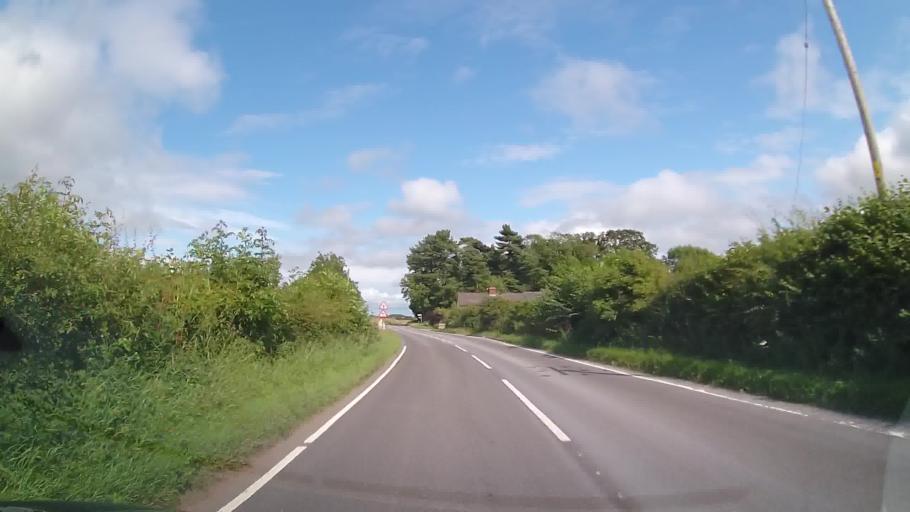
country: GB
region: England
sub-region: Shropshire
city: Pant
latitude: 52.8102
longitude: -3.0404
